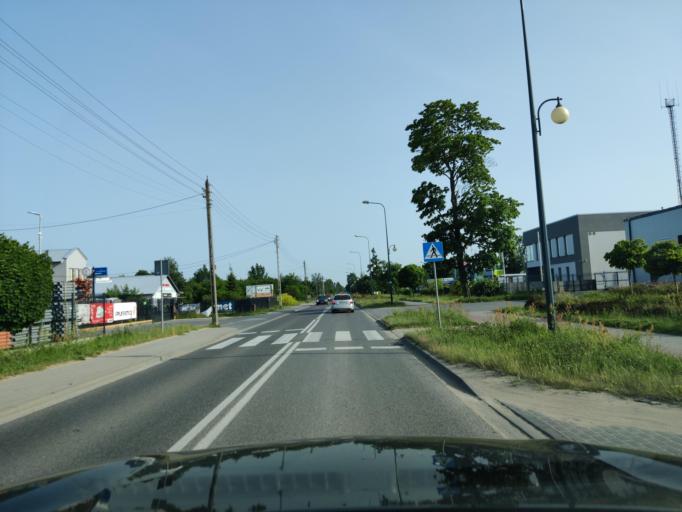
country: PL
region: Masovian Voivodeship
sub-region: Powiat wyszkowski
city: Wyszkow
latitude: 52.6150
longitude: 21.4531
